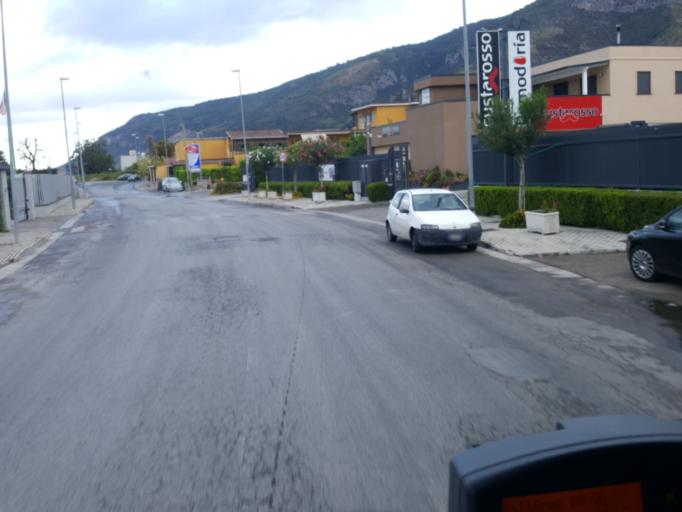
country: IT
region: Campania
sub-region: Provincia di Napoli
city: Striano
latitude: 40.8220
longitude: 14.5994
